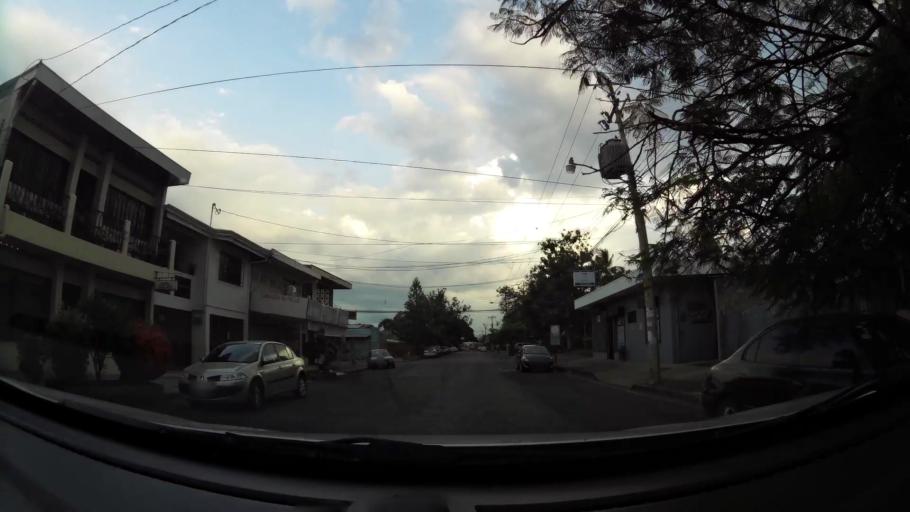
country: CR
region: Puntarenas
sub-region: Canton Central de Puntarenas
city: Puntarenas
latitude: 9.9781
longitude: -84.8354
